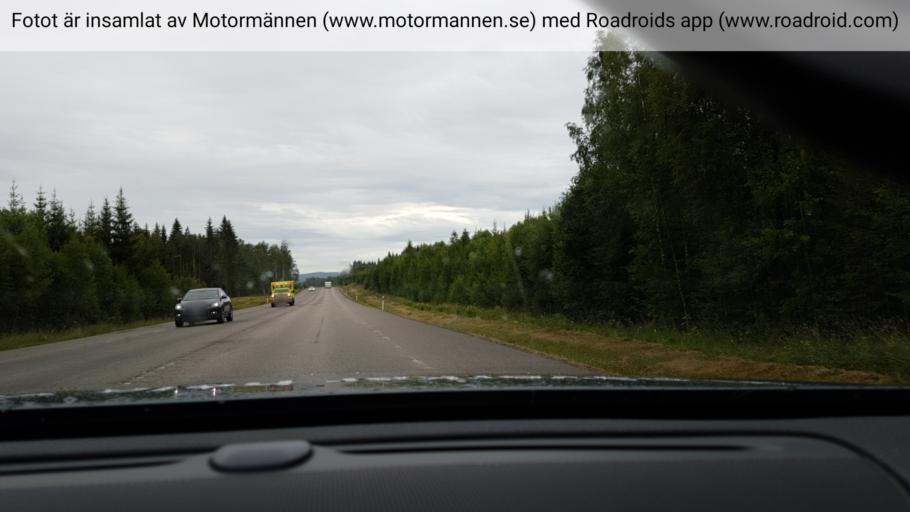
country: SE
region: Dalarna
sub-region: Leksand Municipality
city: Leksand
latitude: 60.7781
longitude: 15.0293
